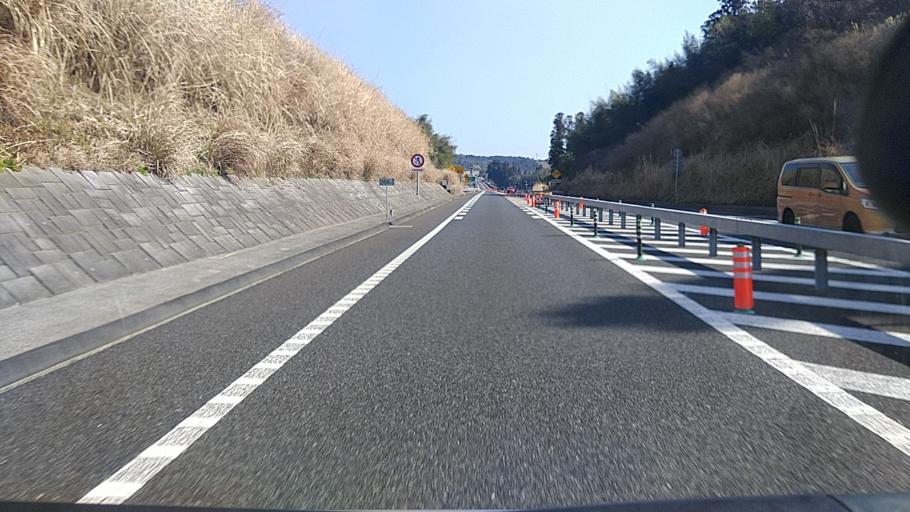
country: JP
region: Chiba
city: Ichihara
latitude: 35.3611
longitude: 140.1424
